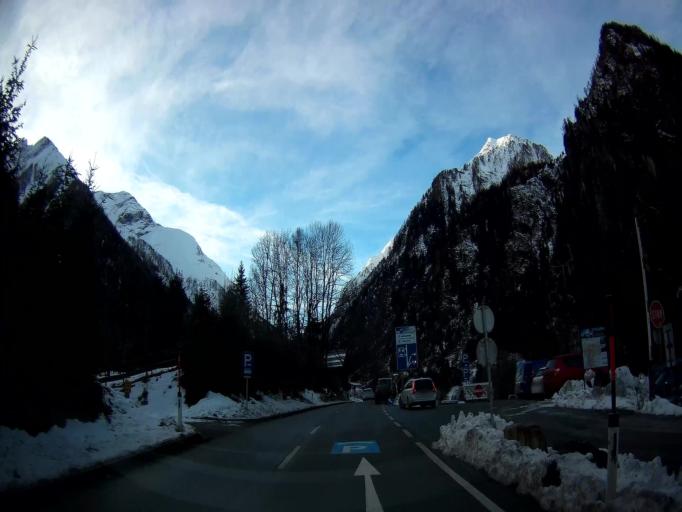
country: AT
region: Salzburg
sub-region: Politischer Bezirk Zell am See
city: Kaprun
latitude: 47.2317
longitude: 12.7278
